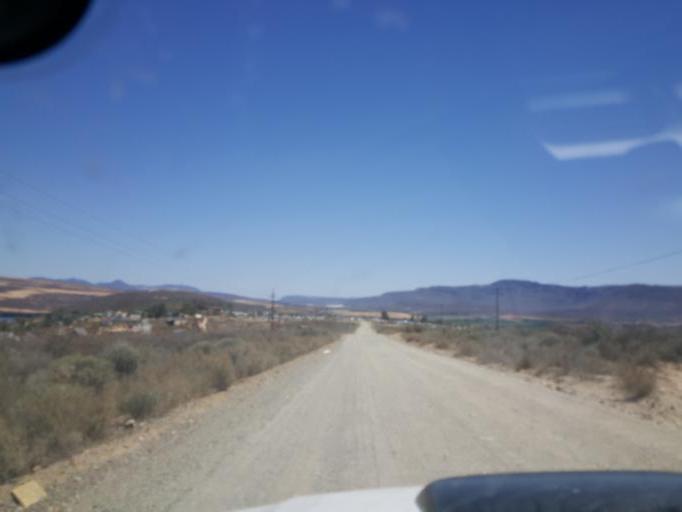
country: ZA
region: Western Cape
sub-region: West Coast District Municipality
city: Clanwilliam
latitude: -32.2013
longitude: 18.8959
